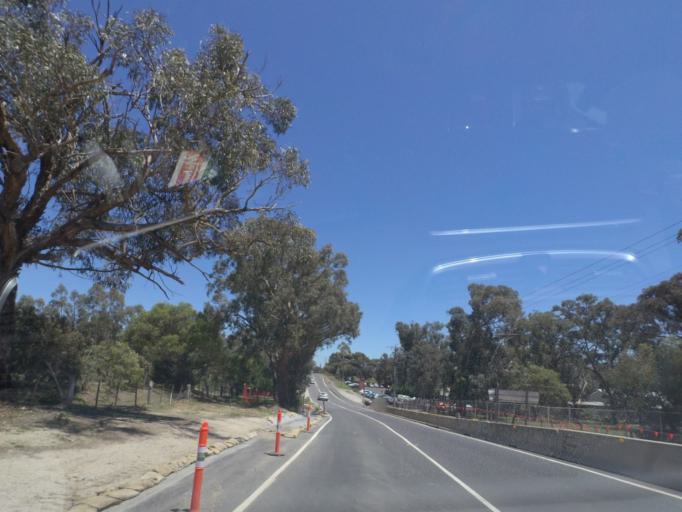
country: AU
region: Victoria
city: Plenty
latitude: -37.6504
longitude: 145.1198
